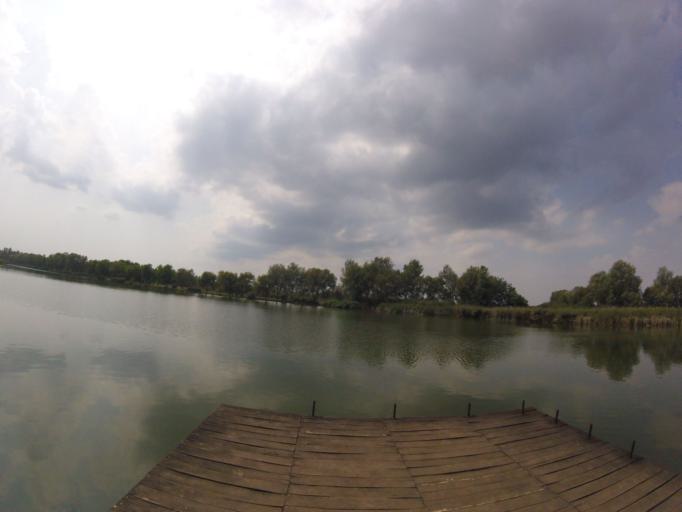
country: HU
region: Szabolcs-Szatmar-Bereg
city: Apagy
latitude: 47.9866
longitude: 21.9483
